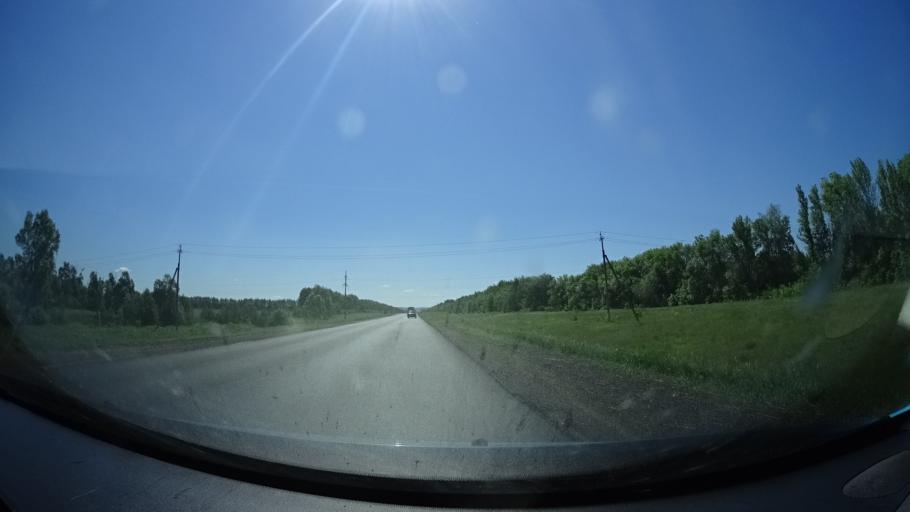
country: RU
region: Bashkortostan
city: Birsk
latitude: 55.2446
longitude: 55.7637
